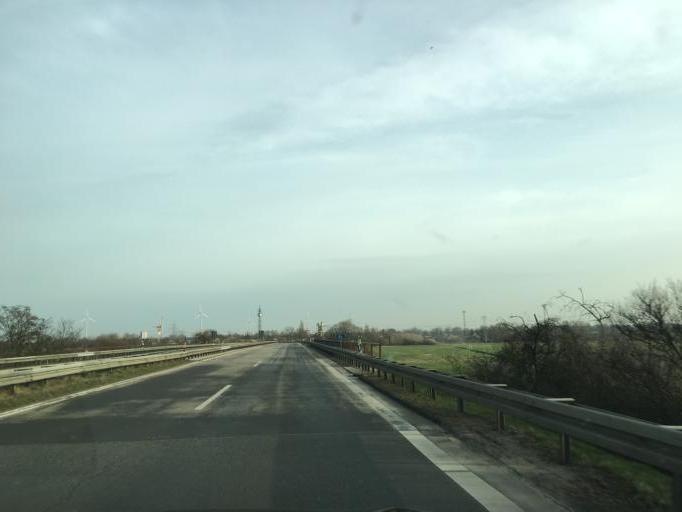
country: DE
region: Berlin
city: Buchholz
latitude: 52.6425
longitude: 13.4266
